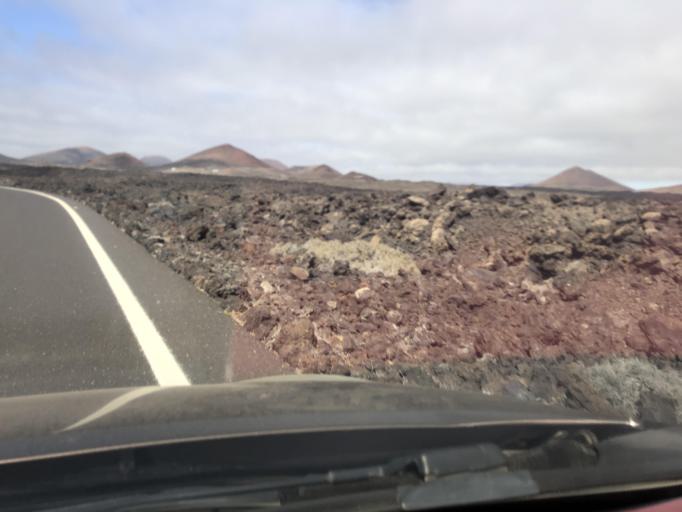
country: ES
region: Canary Islands
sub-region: Provincia de Las Palmas
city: Yaiza
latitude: 28.9766
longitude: -13.8232
